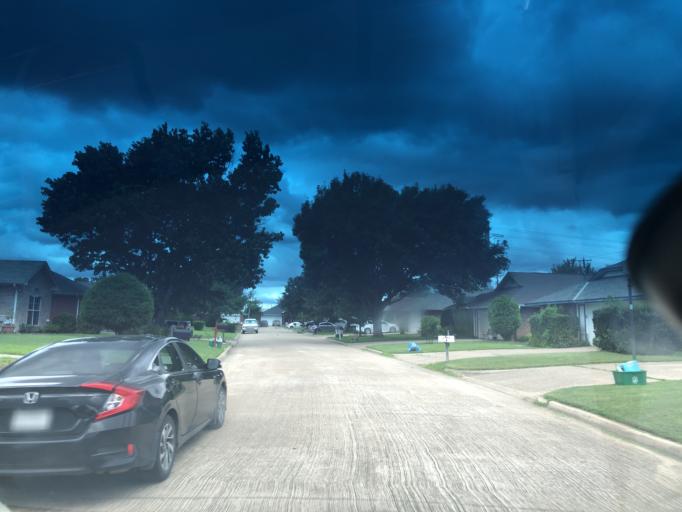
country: US
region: Texas
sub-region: Dallas County
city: Grand Prairie
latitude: 32.6977
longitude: -97.0208
